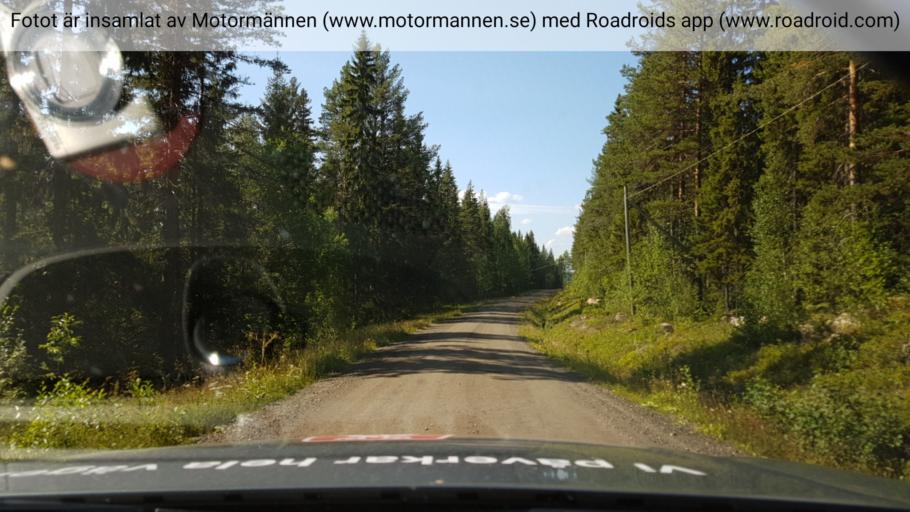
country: SE
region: Vaesterbotten
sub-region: Dorotea Kommun
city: Dorotea
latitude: 64.0851
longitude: 16.5430
